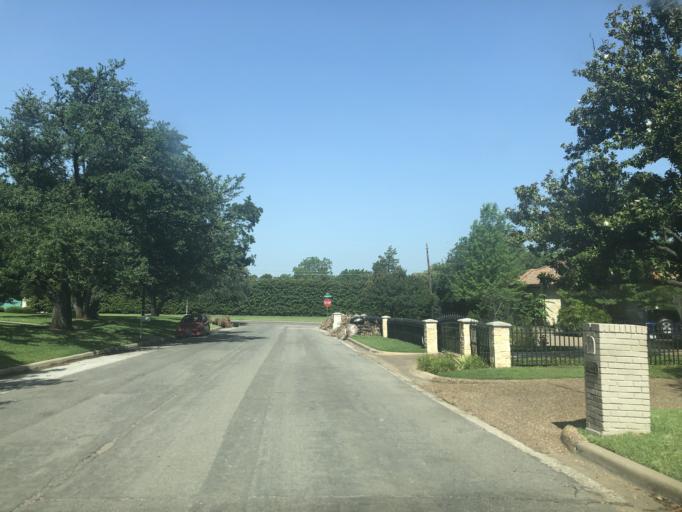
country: US
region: Texas
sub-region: Dallas County
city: University Park
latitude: 32.8865
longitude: -96.8200
